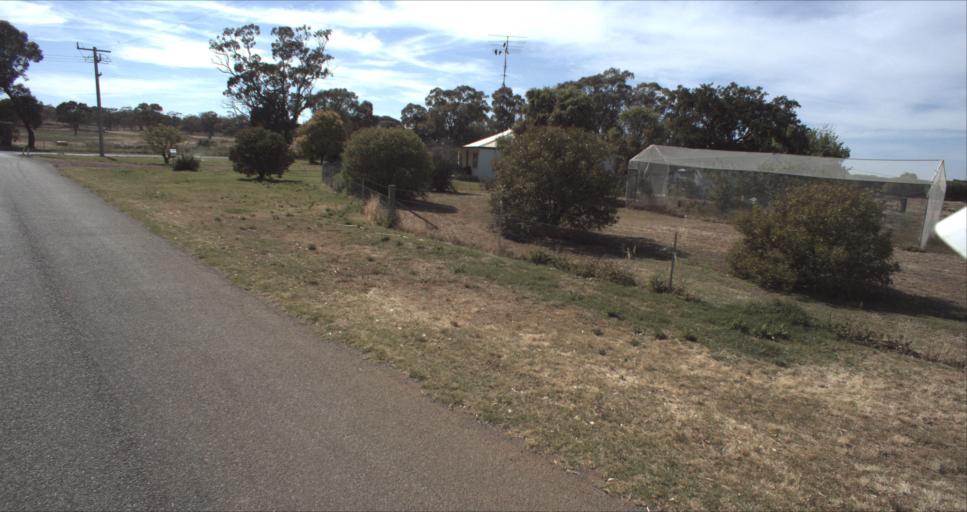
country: AU
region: New South Wales
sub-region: Leeton
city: Leeton
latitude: -34.5868
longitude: 146.4764
